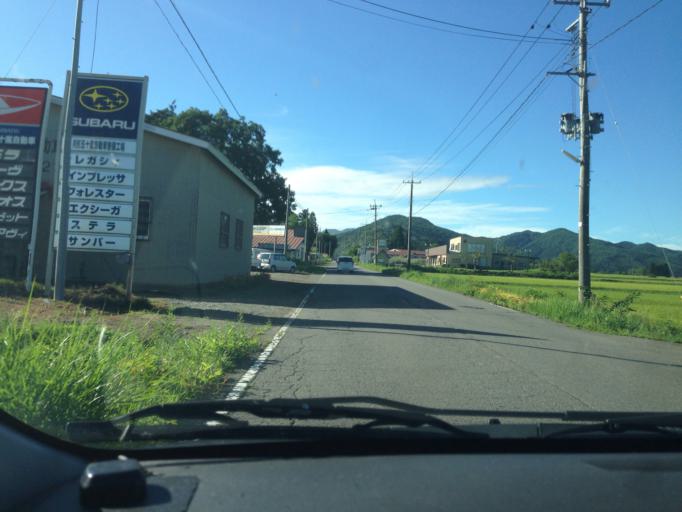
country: JP
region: Fukushima
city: Inawashiro
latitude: 37.4041
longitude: 140.1286
